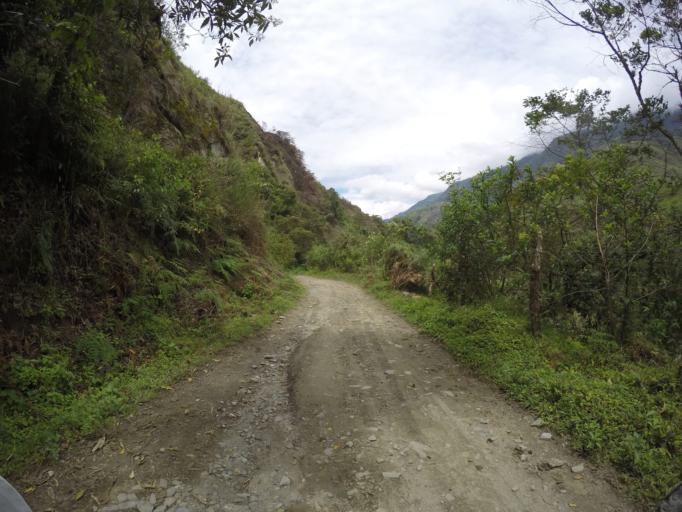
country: CO
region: Tolima
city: Cajamarca
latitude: 4.5240
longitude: -75.4082
